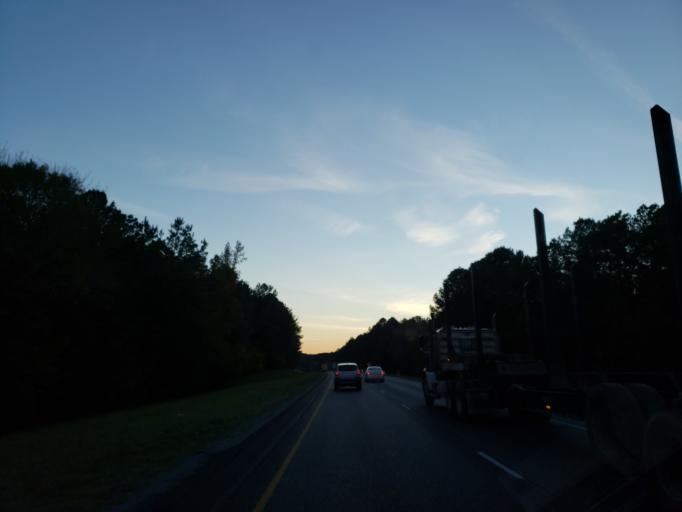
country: US
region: Alabama
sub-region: Sumter County
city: York
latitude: 32.5412
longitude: -88.2809
